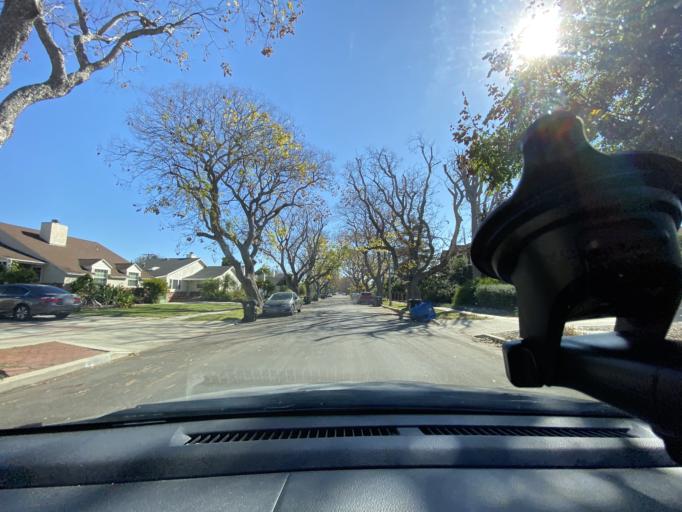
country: US
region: California
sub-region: Los Angeles County
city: Westwood, Los Angeles
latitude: 34.0237
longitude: -118.4319
